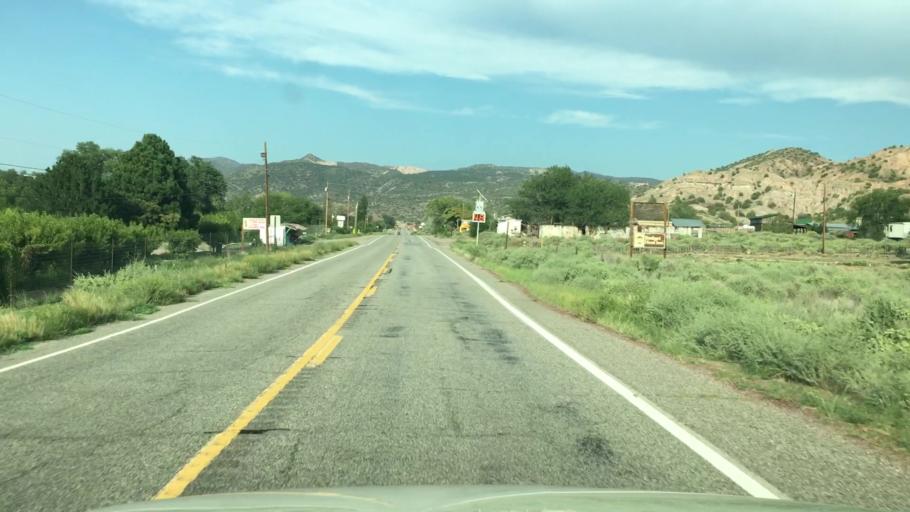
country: US
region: New Mexico
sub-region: Rio Arriba County
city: Chimayo
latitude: 36.2151
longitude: -105.8853
